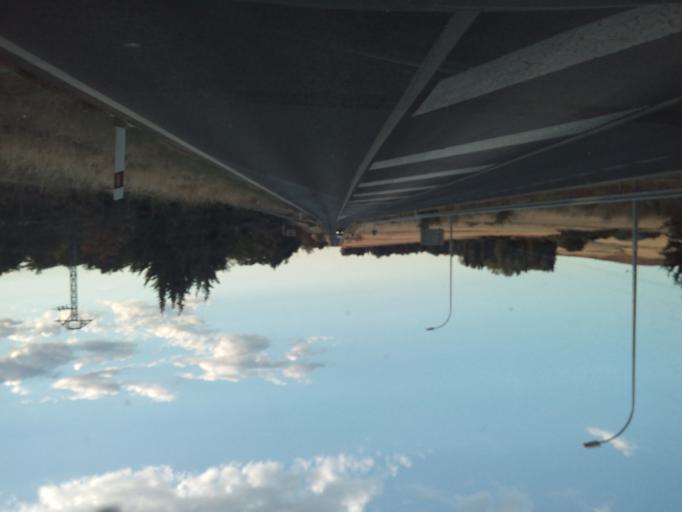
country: ES
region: Madrid
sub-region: Provincia de Madrid
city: Algete
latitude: 40.6210
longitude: -3.4806
